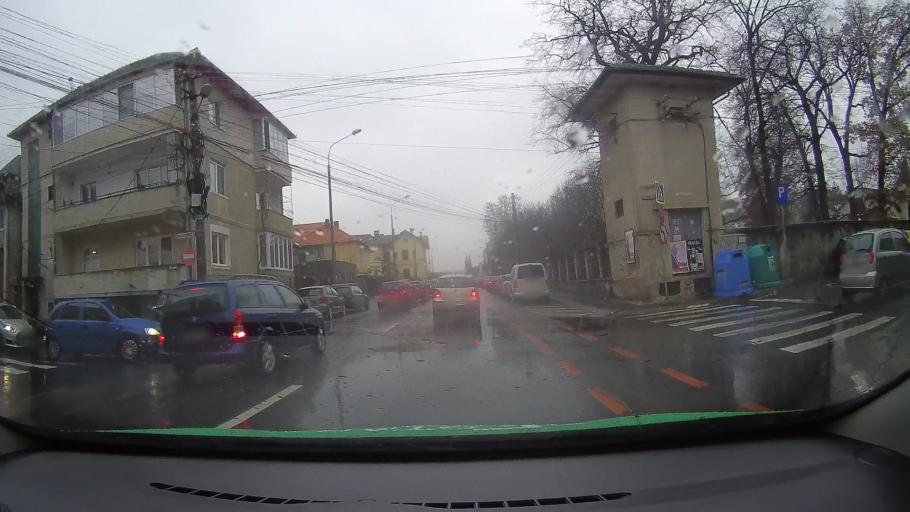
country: RO
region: Sibiu
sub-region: Municipiul Sibiu
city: Sibiu
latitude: 45.7893
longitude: 24.1411
